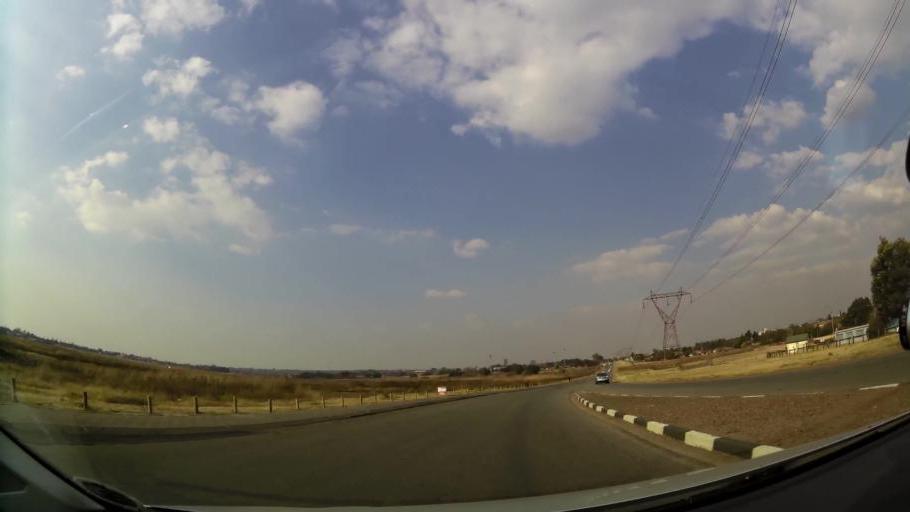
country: ZA
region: Gauteng
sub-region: City of Johannesburg Metropolitan Municipality
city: Modderfontein
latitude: -26.1085
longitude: 28.1986
